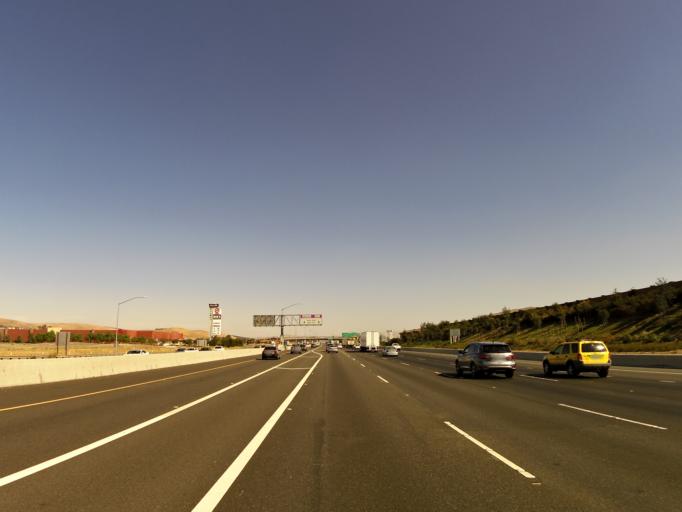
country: US
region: California
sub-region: Alameda County
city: Pleasanton
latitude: 37.7008
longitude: -121.8581
